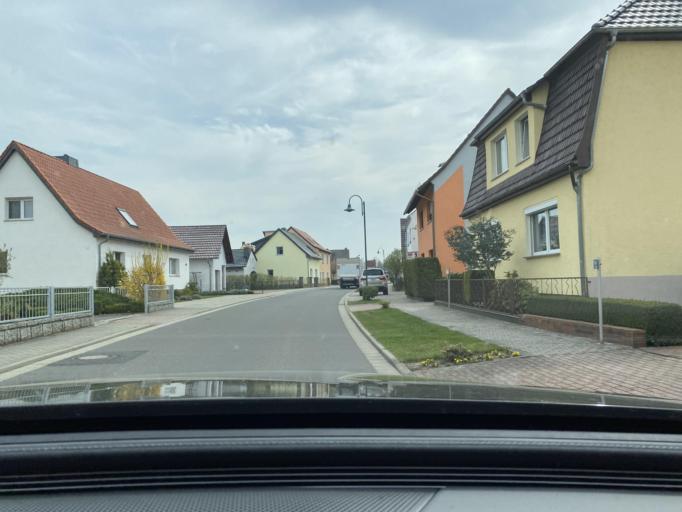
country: DE
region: Saxony
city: Wittichenau
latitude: 51.3787
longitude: 14.2547
